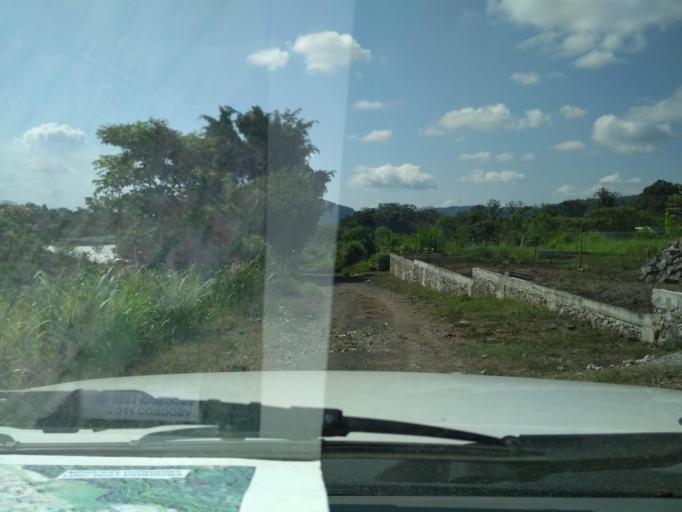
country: MX
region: Veracruz
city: Amatlan de los Reyes
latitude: 18.8657
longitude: -96.9067
